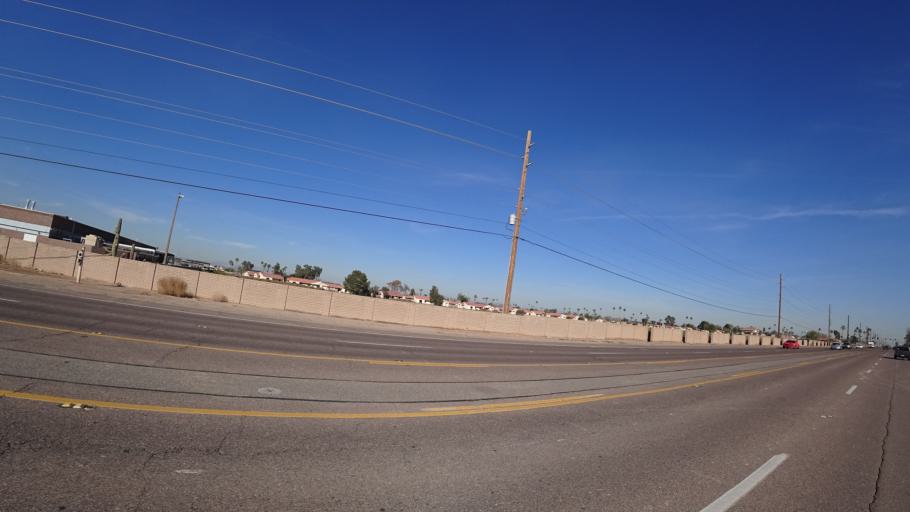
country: US
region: Arizona
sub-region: Maricopa County
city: Litchfield Park
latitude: 33.5368
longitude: -112.3543
